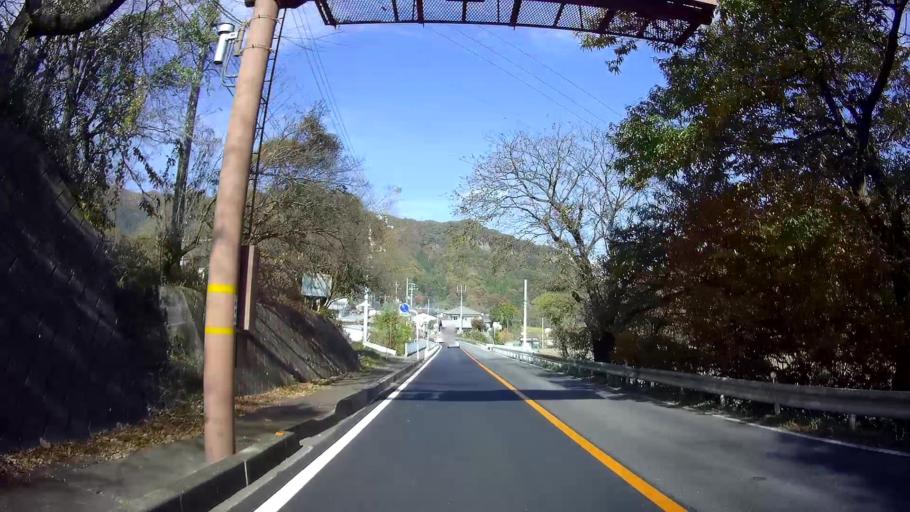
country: JP
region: Gunma
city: Nakanojomachi
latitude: 36.5088
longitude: 138.7755
